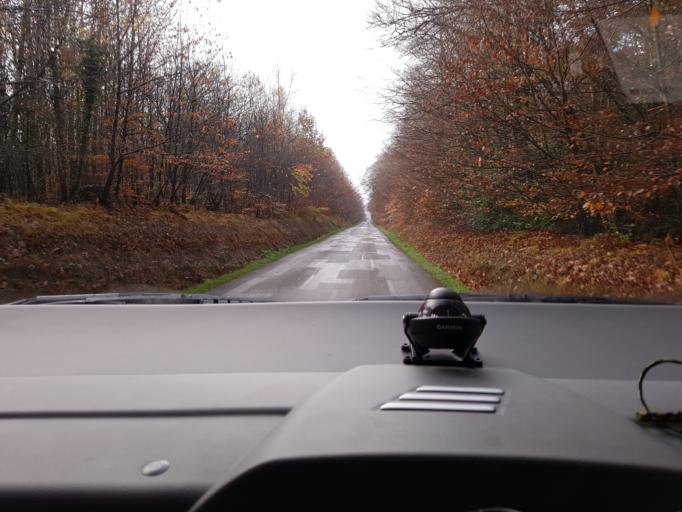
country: FR
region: Brittany
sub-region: Departement d'Ille-et-Vilaine
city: Saint-Sulpice-la-Foret
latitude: 48.1968
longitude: -1.6001
